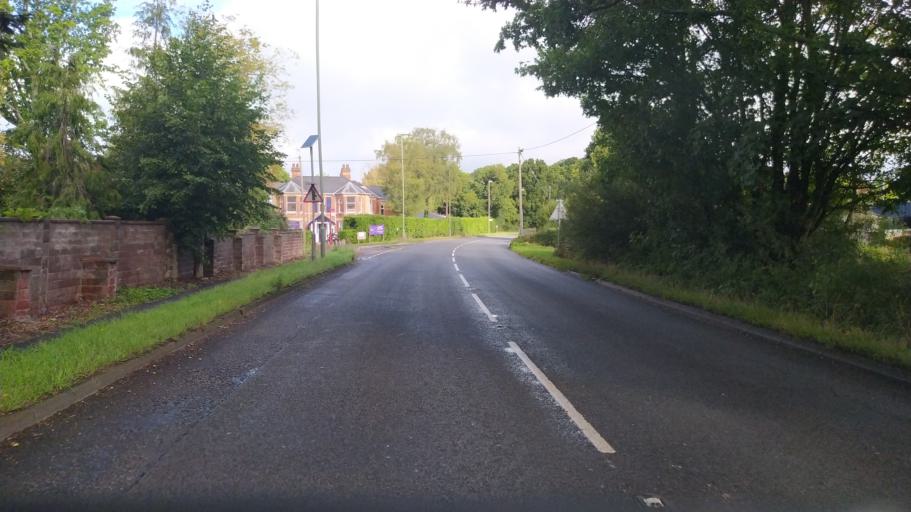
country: GB
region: England
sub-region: Hampshire
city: Totton
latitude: 50.9338
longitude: -1.5108
